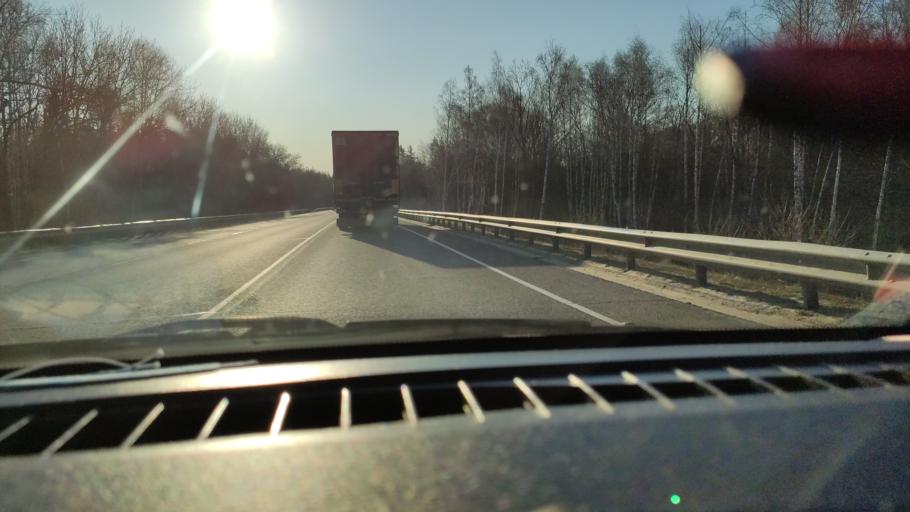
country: RU
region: Saratov
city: Vol'sk
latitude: 52.1065
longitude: 47.4271
